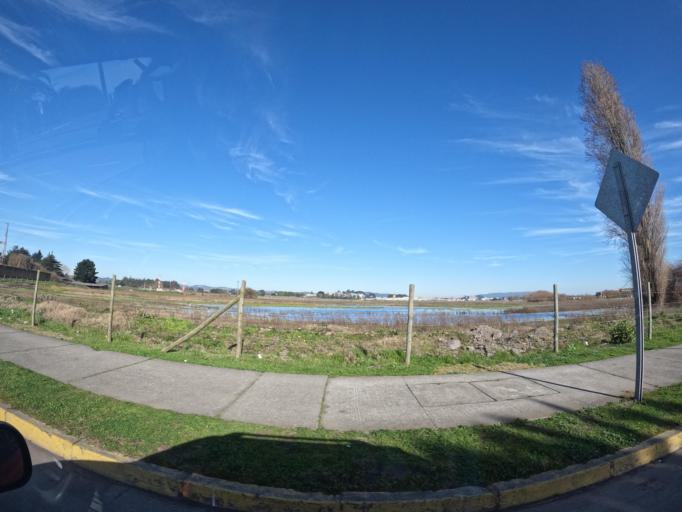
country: CL
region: Biobio
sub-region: Provincia de Concepcion
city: Concepcion
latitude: -36.7771
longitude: -73.0719
